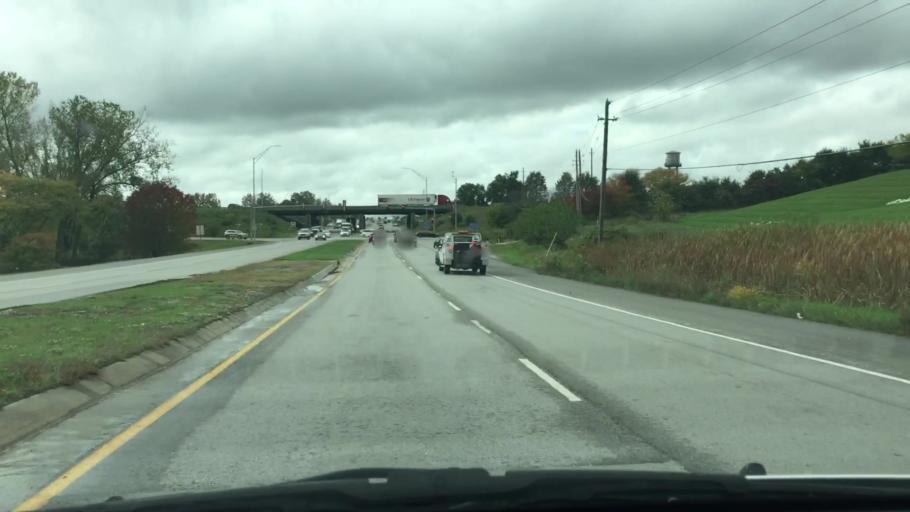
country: US
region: Iowa
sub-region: Polk County
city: Clive
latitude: 41.6150
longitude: -93.7735
